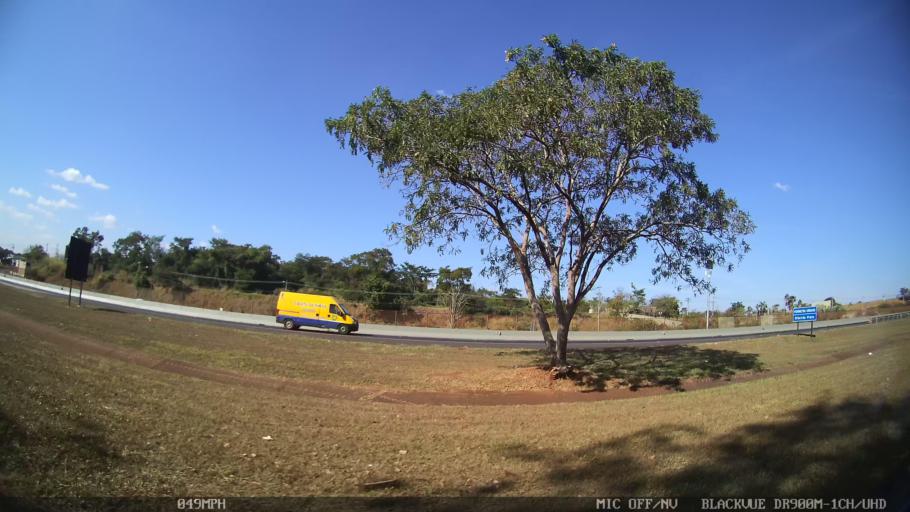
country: BR
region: Sao Paulo
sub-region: Ribeirao Preto
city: Ribeirao Preto
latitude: -21.1624
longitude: -47.7565
